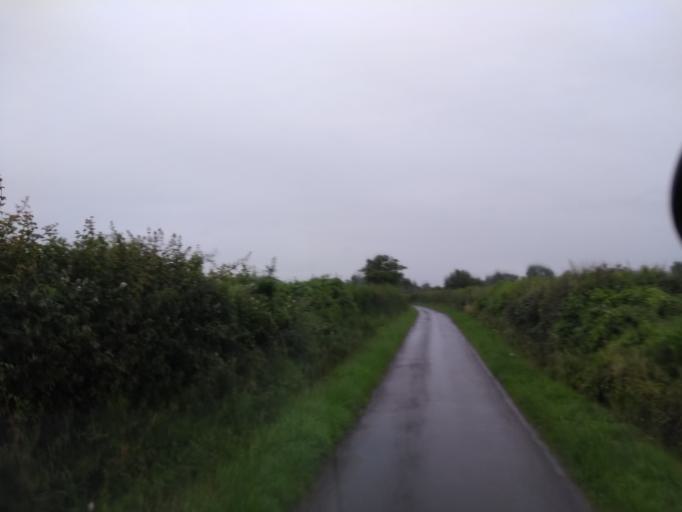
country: GB
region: England
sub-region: Somerset
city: Street
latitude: 51.0976
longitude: -2.6966
